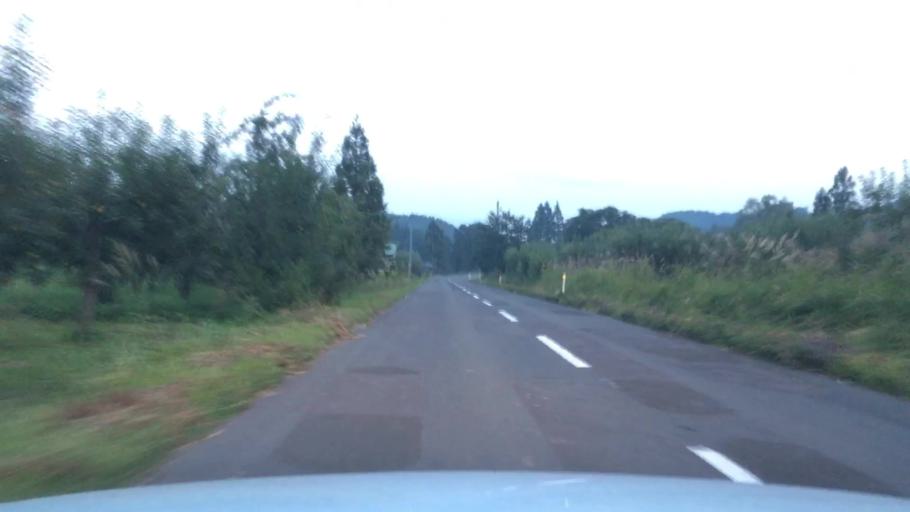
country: JP
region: Aomori
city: Hirosaki
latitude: 40.6757
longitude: 140.3822
